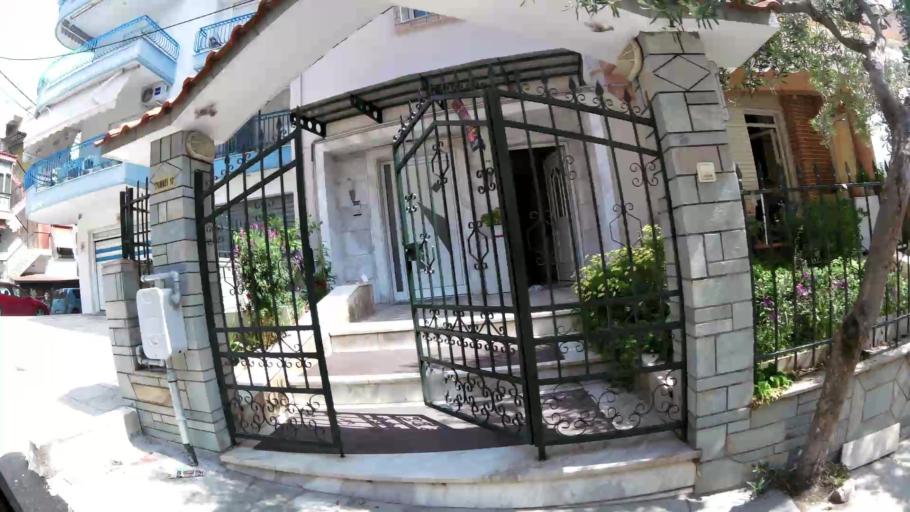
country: GR
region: Central Macedonia
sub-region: Nomos Thessalonikis
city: Stavroupoli
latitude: 40.6752
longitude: 22.9309
